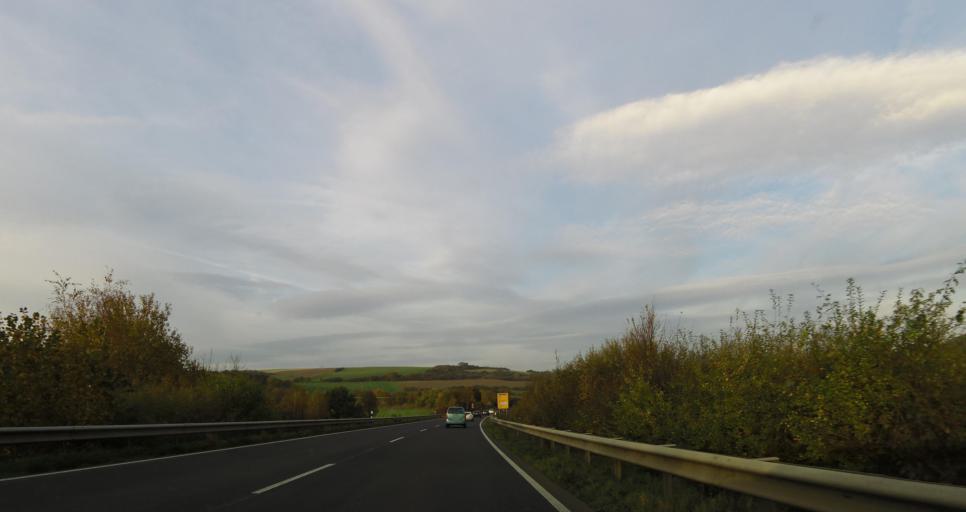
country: DE
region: Lower Saxony
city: Einbeck
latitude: 51.8309
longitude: 9.8309
